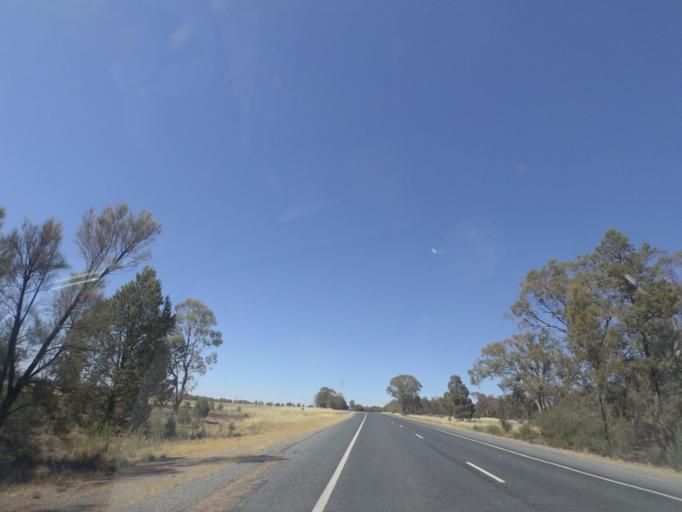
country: AU
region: New South Wales
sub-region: Narrandera
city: Narrandera
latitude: -34.4450
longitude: 146.8401
